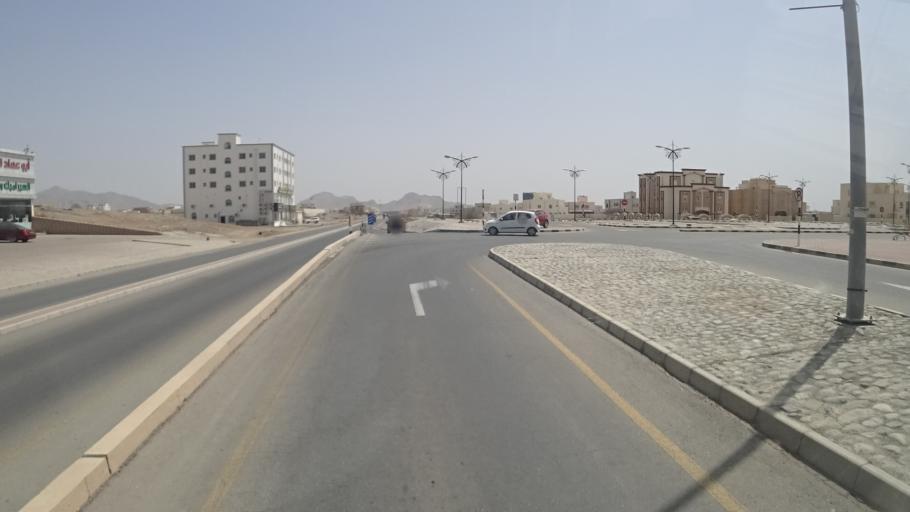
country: OM
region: Muhafazat ad Dakhiliyah
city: Nizwa
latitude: 22.8757
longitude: 57.5398
